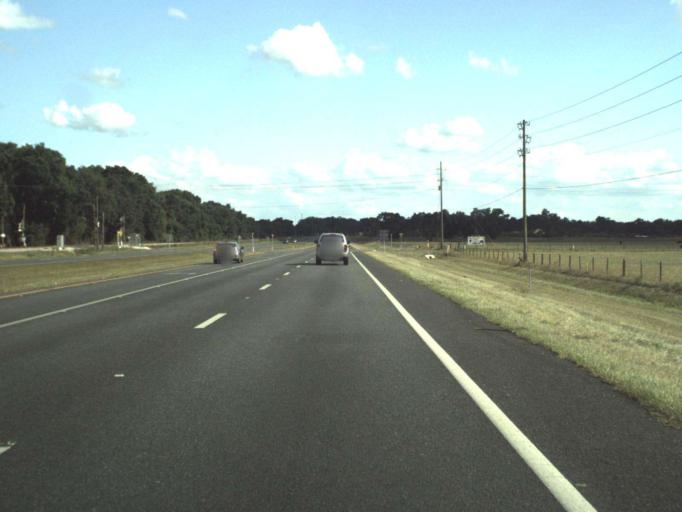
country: US
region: Florida
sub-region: Sumter County
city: The Villages
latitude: 28.9471
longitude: -82.0386
